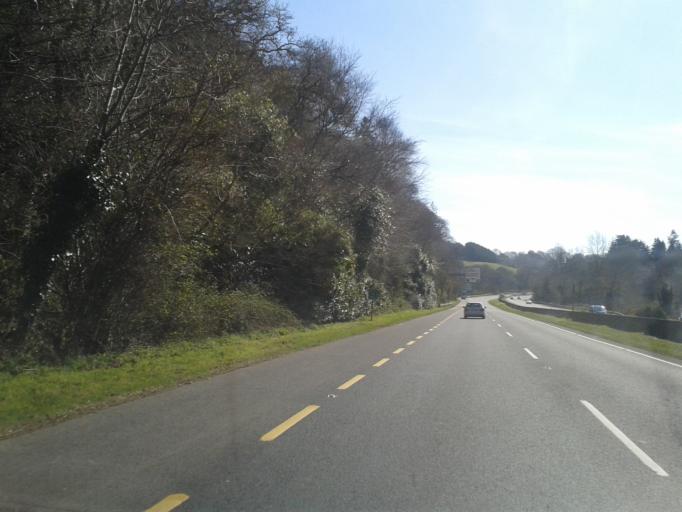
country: IE
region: Leinster
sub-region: Wicklow
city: Kilpedder
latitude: 53.1316
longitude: -6.1093
